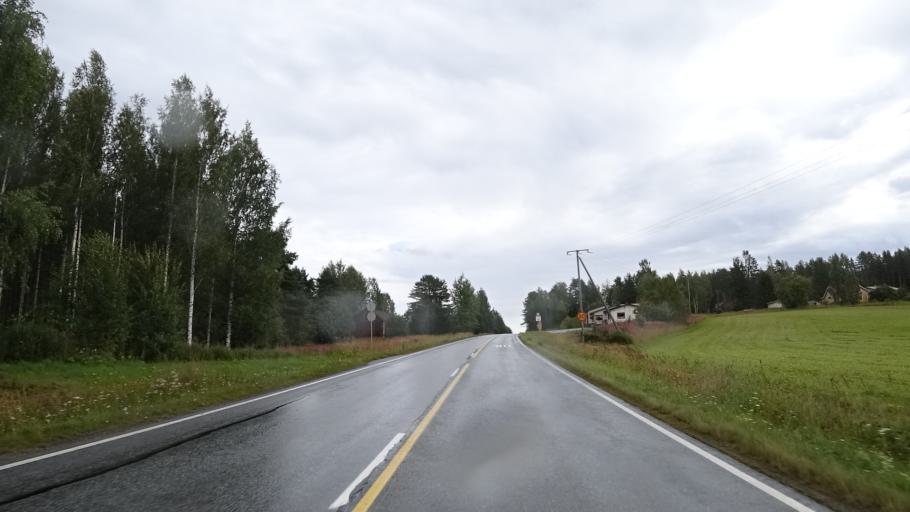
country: FI
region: North Karelia
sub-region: Keski-Karjala
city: Raeaekkylae
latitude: 62.0463
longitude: 29.5607
